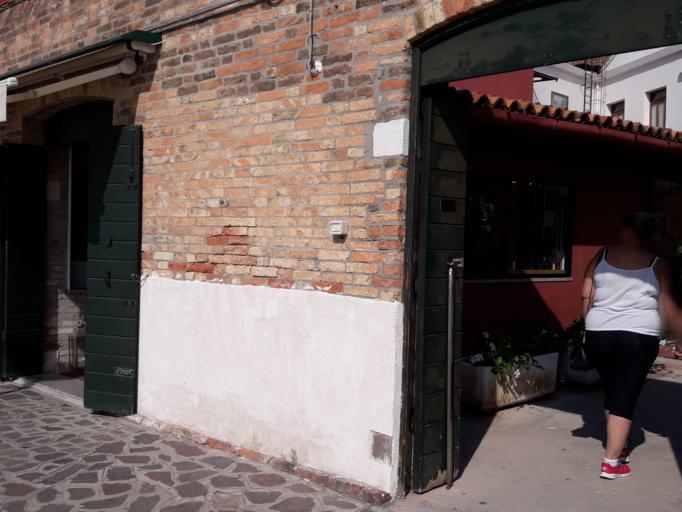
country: IT
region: Veneto
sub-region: Provincia di Venezia
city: Murano
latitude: 45.4523
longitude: 12.3480
